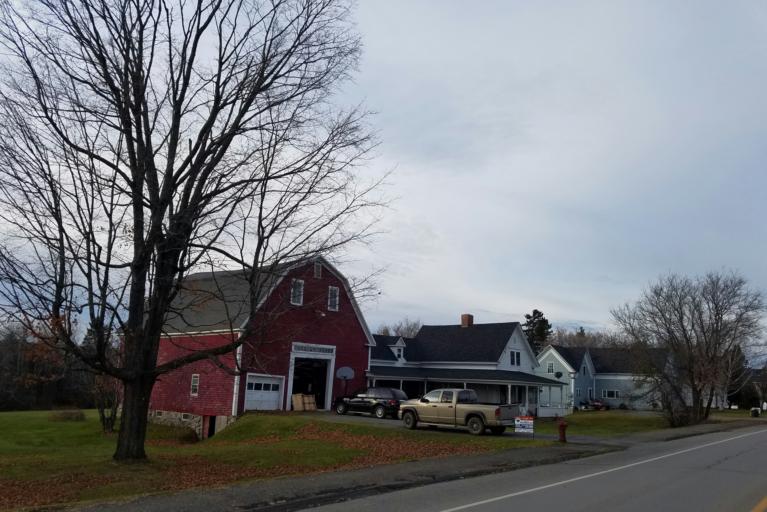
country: US
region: Maine
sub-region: Aroostook County
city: Caribou
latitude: 46.7861
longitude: -68.1566
